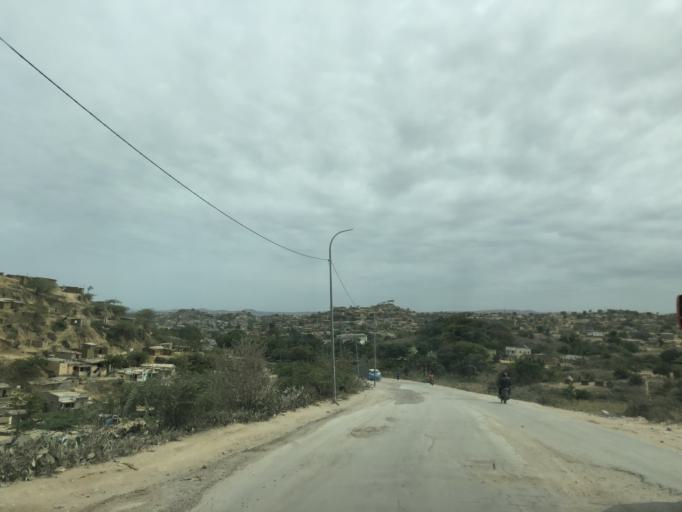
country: AO
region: Cuanza Sul
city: Sumbe
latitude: -11.2220
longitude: 13.8473
